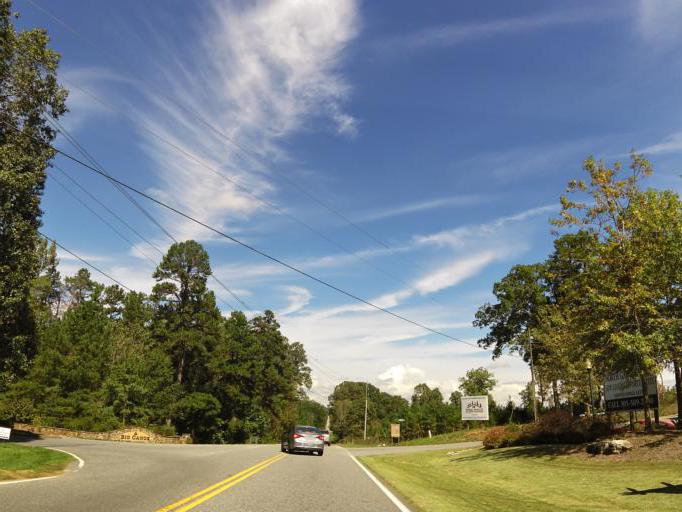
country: US
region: Georgia
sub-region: Pickens County
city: Nelson
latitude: 34.4614
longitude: -84.2603
